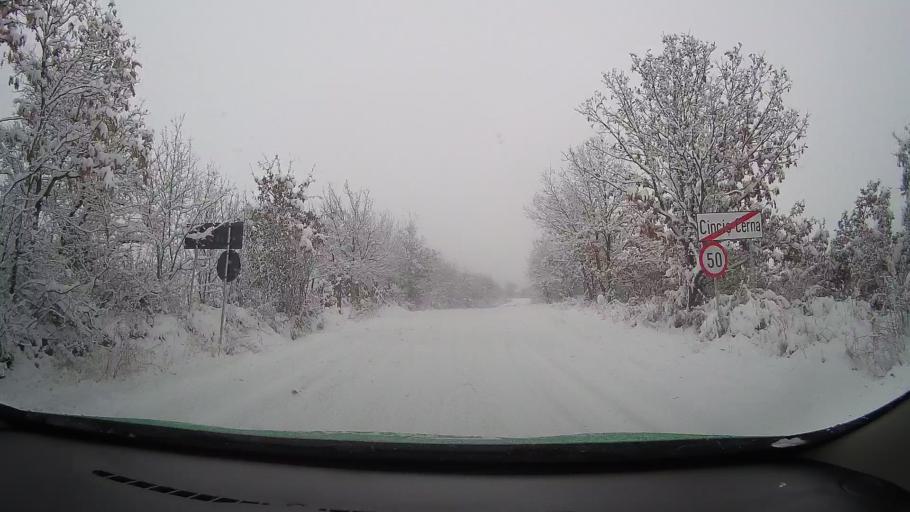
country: RO
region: Hunedoara
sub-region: Comuna Teliucu Inferior
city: Teliucu Inferior
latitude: 45.6973
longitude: 22.8916
